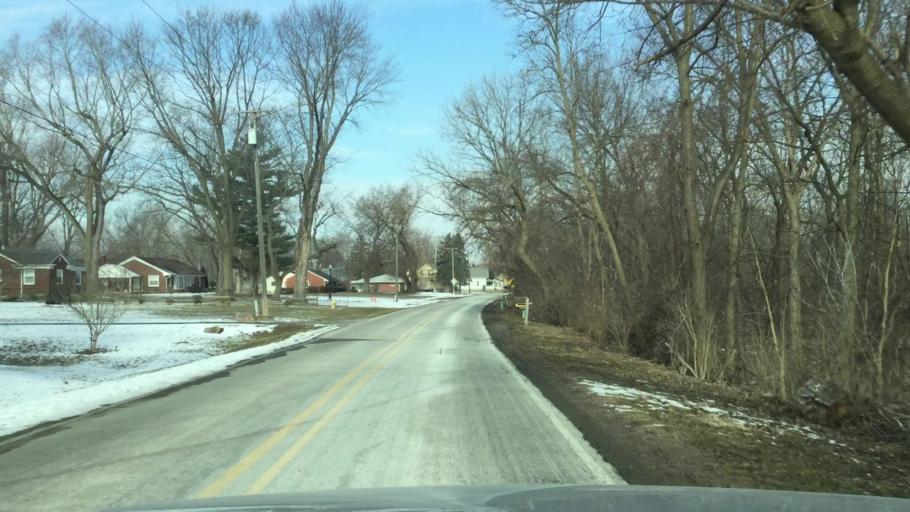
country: US
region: Michigan
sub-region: Wayne County
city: Flat Rock
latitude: 42.0908
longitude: -83.2916
